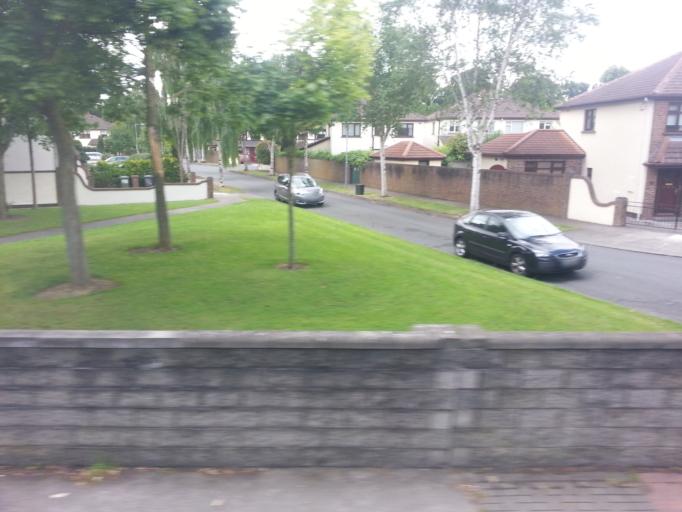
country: IE
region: Leinster
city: Chapelizod
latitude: 53.3711
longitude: -6.3291
